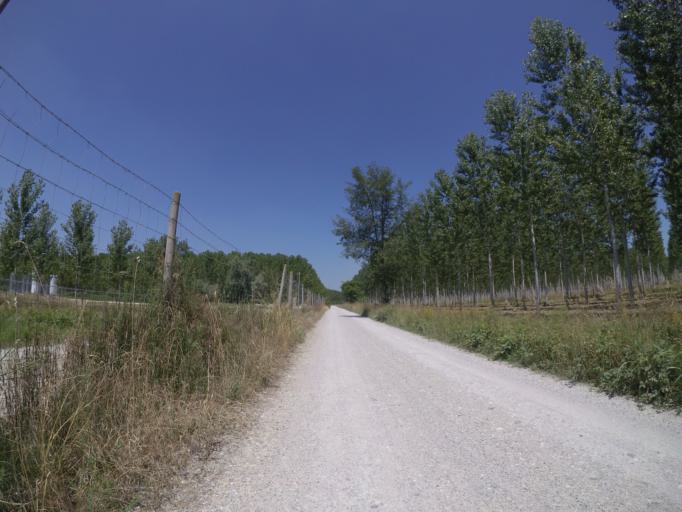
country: IT
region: Friuli Venezia Giulia
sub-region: Provincia di Udine
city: Rivignano
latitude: 45.9129
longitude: 13.0257
